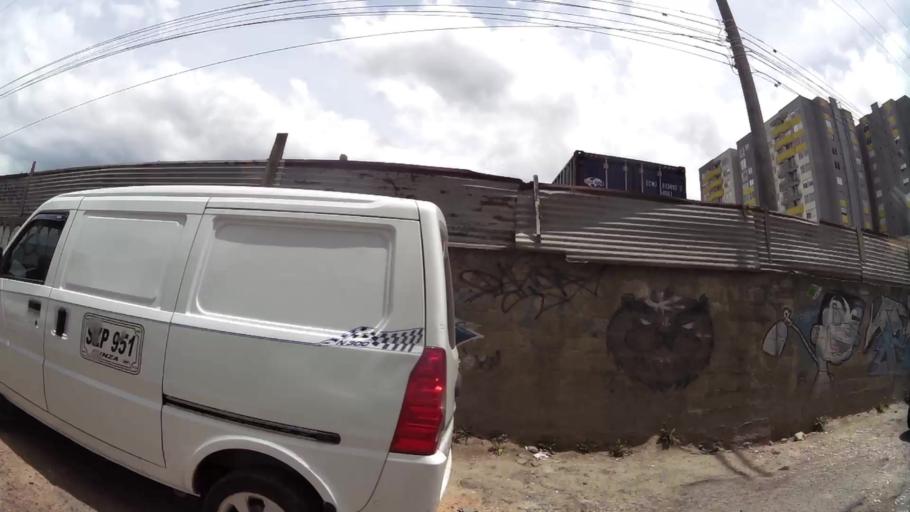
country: CO
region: Bogota D.C.
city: Bogota
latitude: 4.6464
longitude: -74.1444
